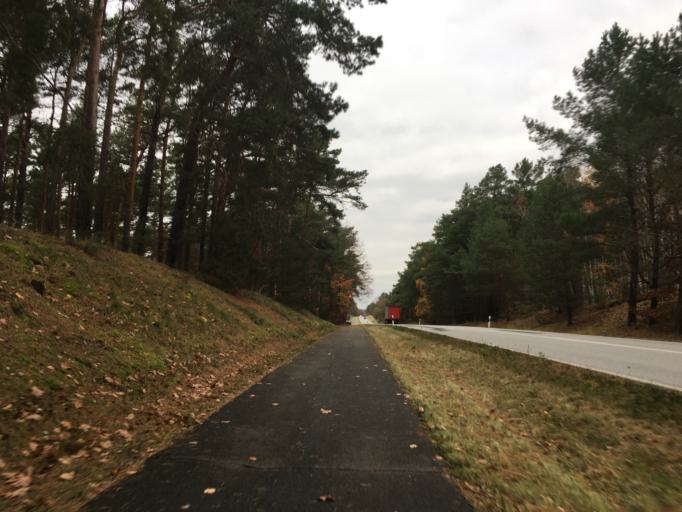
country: DE
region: Brandenburg
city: Mixdorf
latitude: 52.1971
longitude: 14.4602
